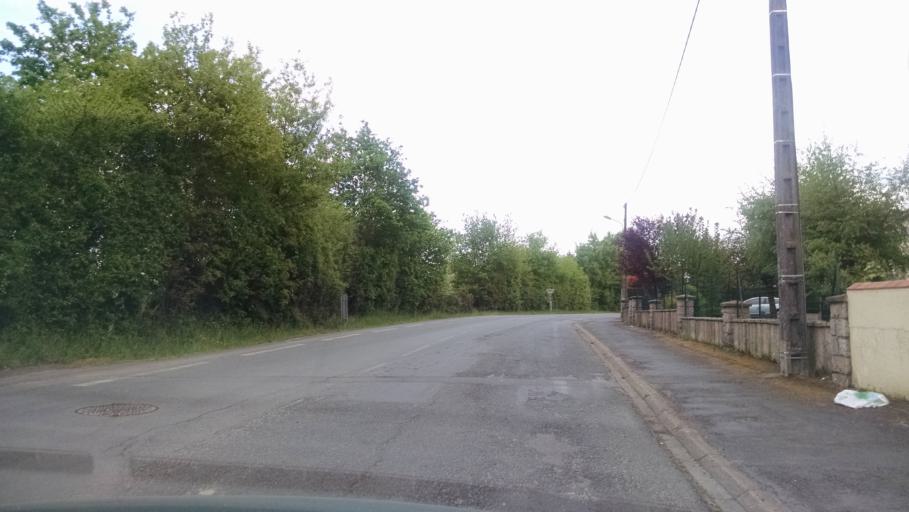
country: FR
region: Pays de la Loire
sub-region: Departement de la Loire-Atlantique
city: Gorges
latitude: 47.0906
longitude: -1.2934
